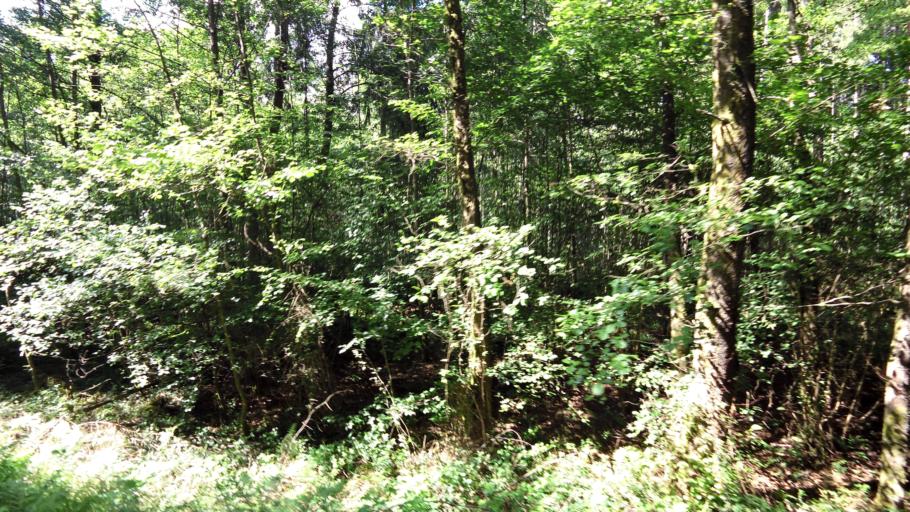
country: FR
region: Lorraine
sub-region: Departement de la Moselle
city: Abreschviller
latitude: 48.6277
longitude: 7.1155
